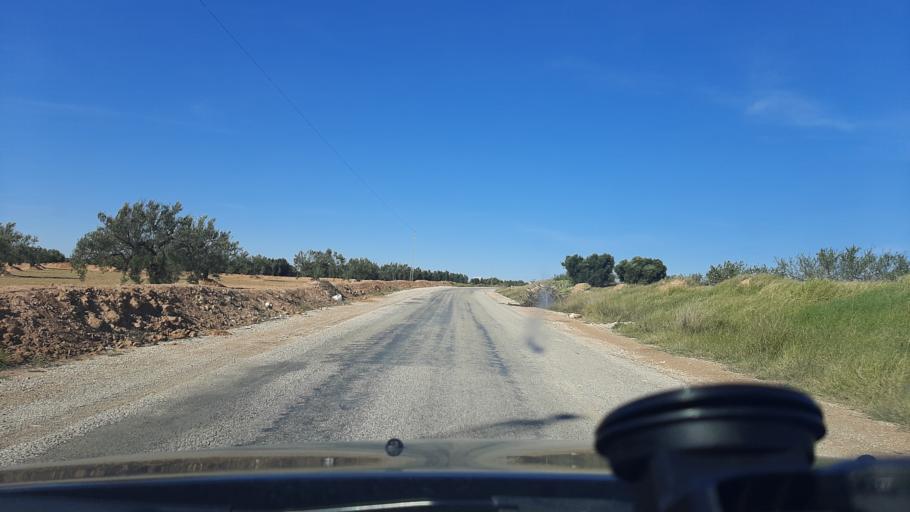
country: TN
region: Safaqis
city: Sfax
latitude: 34.9432
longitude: 10.5545
